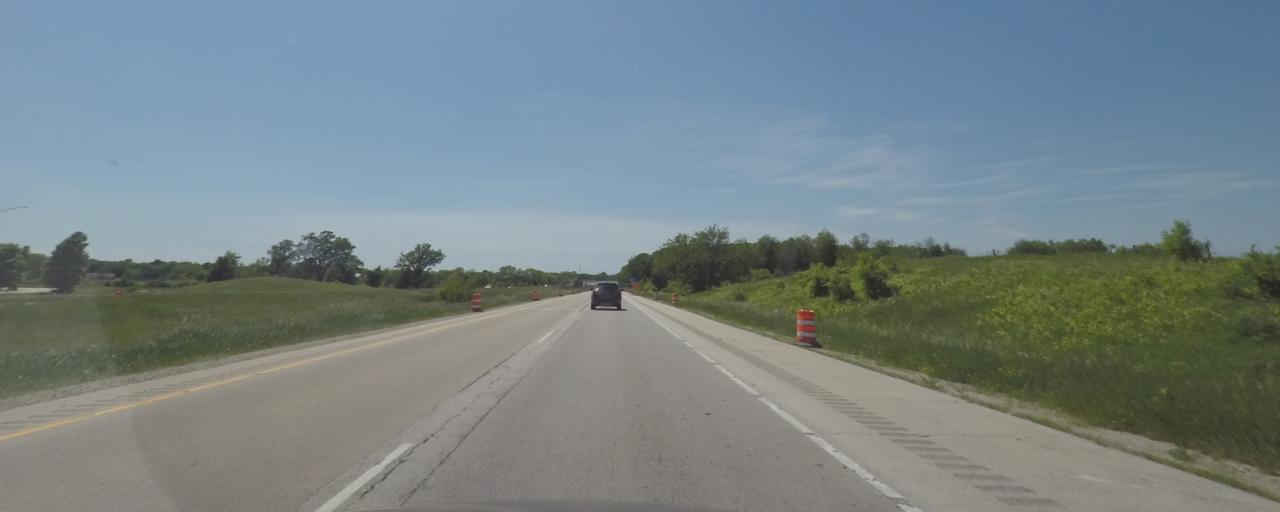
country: US
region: Wisconsin
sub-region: Jefferson County
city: Lake Mills
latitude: 43.0875
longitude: -88.8756
